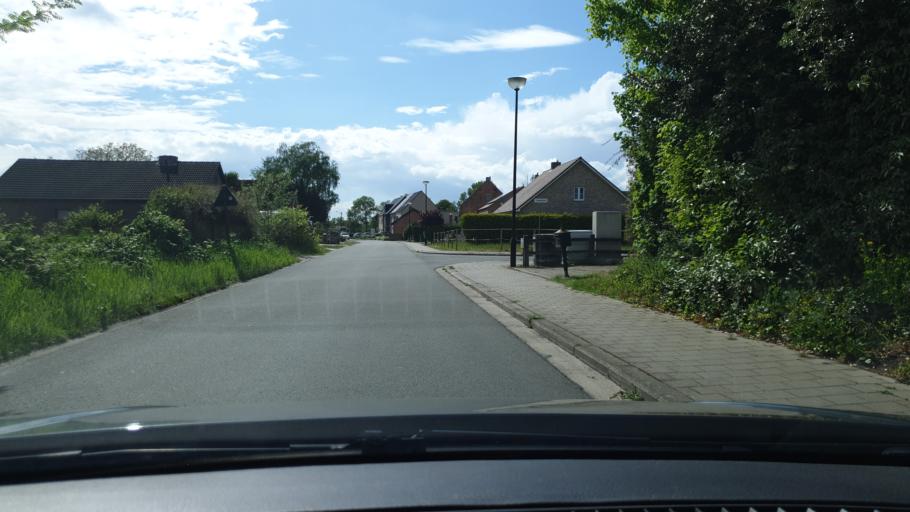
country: BE
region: Flanders
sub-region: Provincie Antwerpen
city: Geel
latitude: 51.2023
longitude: 4.9781
